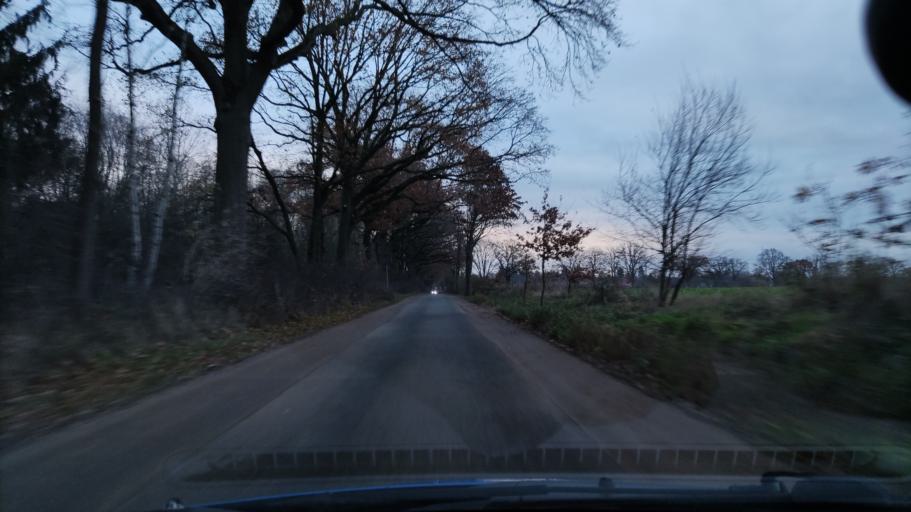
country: DE
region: Lower Saxony
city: Reppenstedt
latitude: 53.2589
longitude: 10.3668
